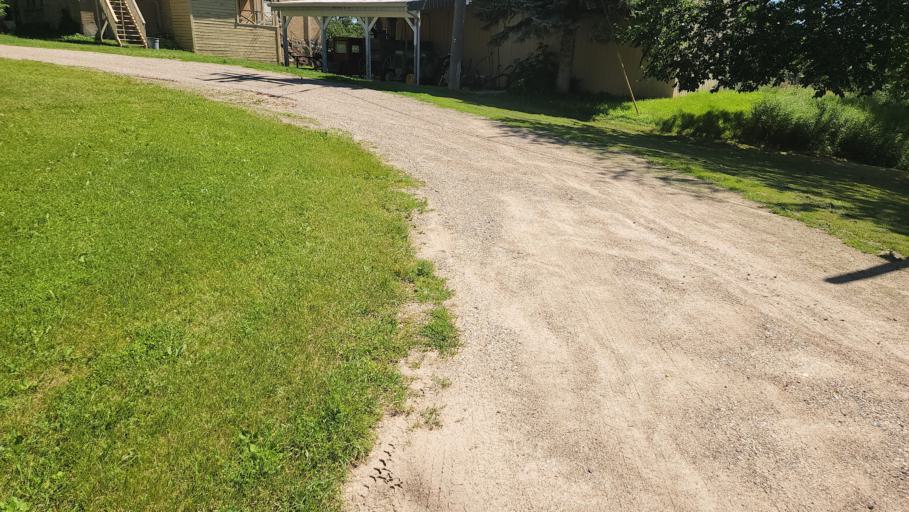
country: CA
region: Manitoba
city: Souris
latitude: 49.6162
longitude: -100.2575
